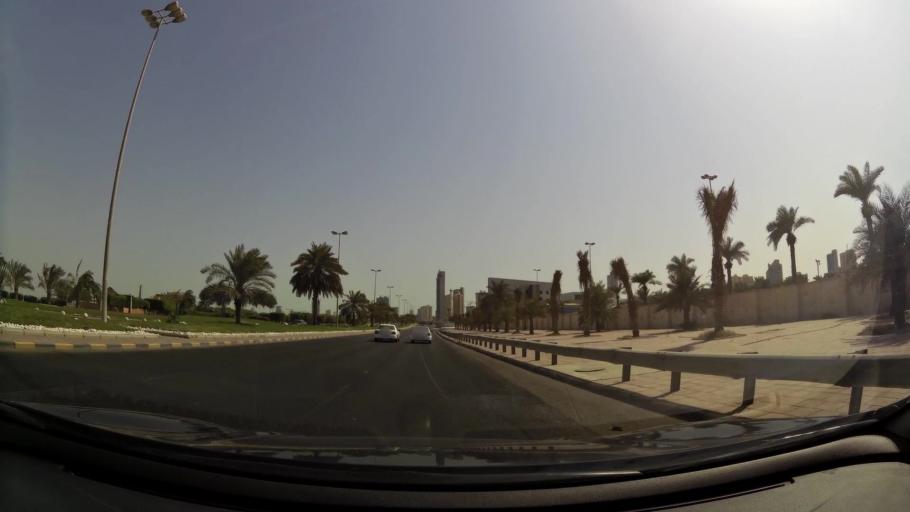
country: KW
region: Muhafazat Hawalli
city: Hawalli
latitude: 29.3473
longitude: 48.0383
